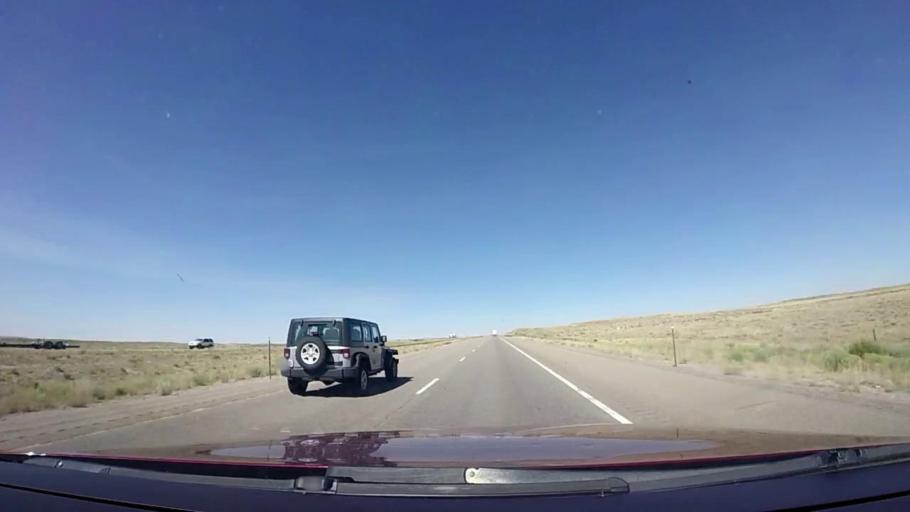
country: US
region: Wyoming
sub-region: Sweetwater County
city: Rock Springs
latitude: 41.6389
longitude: -108.4648
